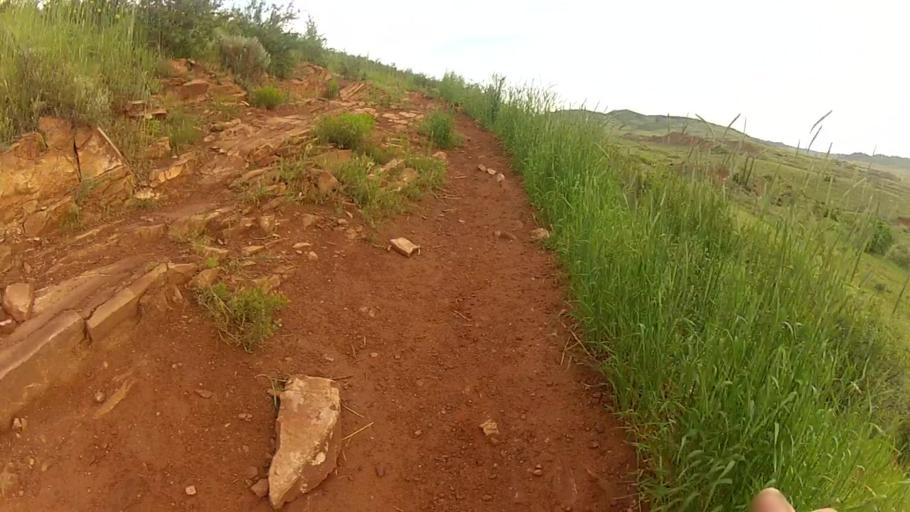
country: US
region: Colorado
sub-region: Larimer County
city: Loveland
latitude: 40.4145
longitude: -105.1537
